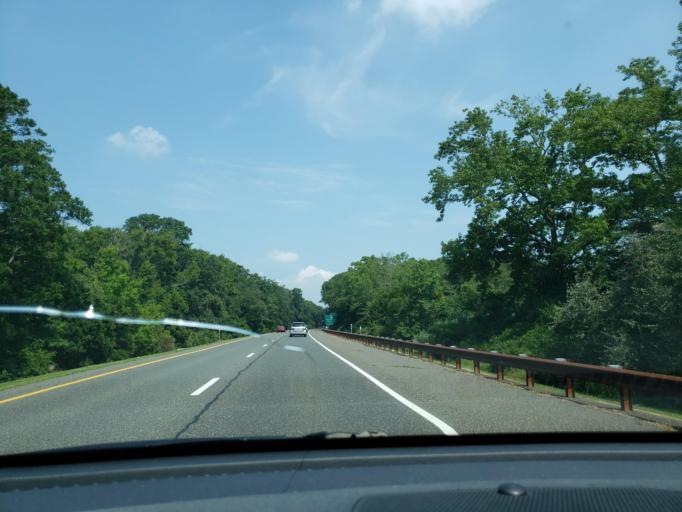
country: US
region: New Jersey
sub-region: Cape May County
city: Rio Grande
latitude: 38.9954
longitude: -74.8778
